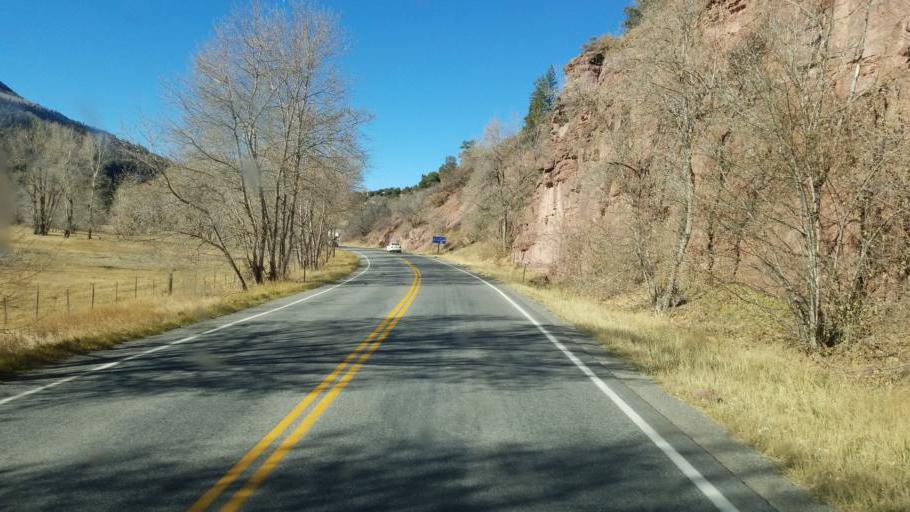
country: US
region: Colorado
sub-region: Ouray County
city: Ouray
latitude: 38.0485
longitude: -107.6825
